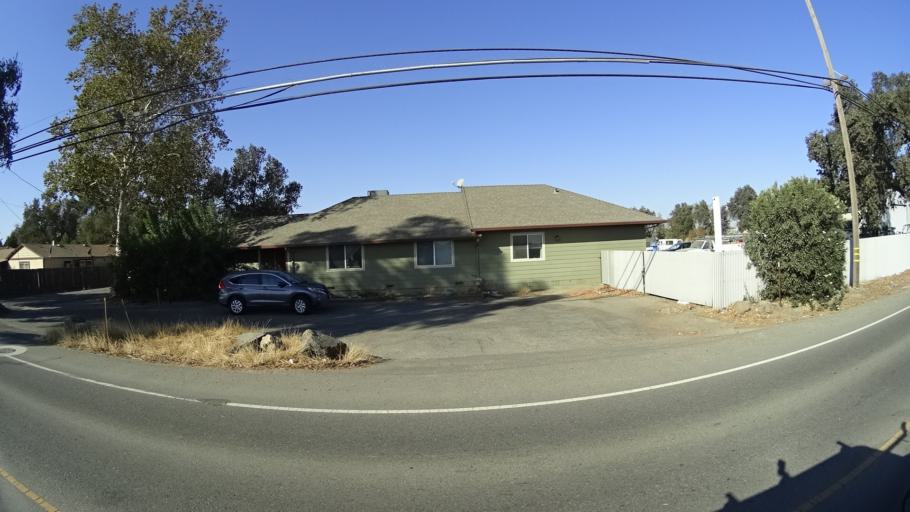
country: US
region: California
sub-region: Yolo County
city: Woodland
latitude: 38.6938
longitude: -121.7839
